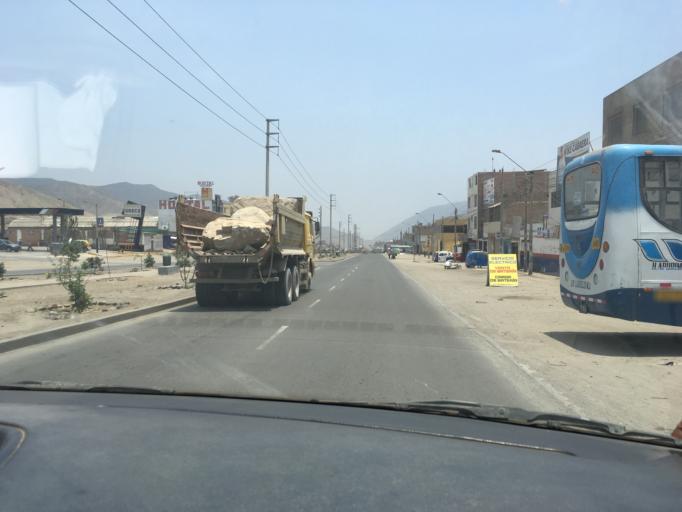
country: PE
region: Lima
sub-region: Lima
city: Cieneguilla
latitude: -12.1186
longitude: -76.8730
